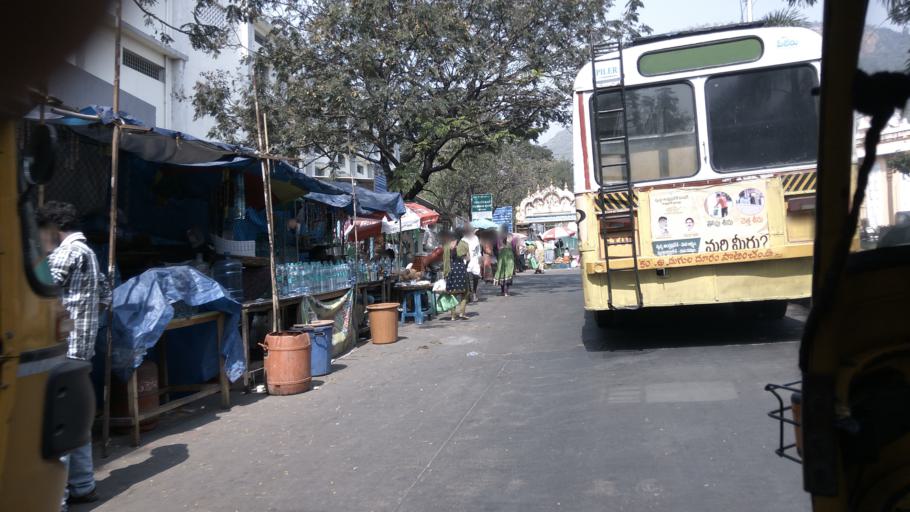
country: IN
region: Andhra Pradesh
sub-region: Chittoor
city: Akkarampalle
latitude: 13.6460
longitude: 79.4061
